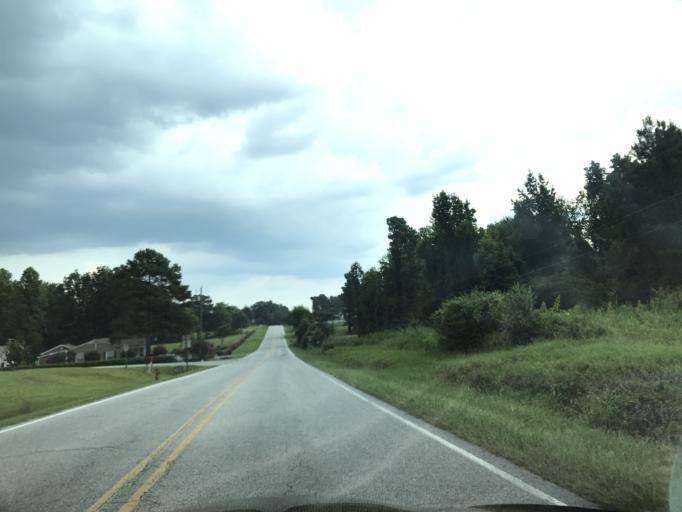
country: US
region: North Carolina
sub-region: Johnston County
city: Four Oaks
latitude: 35.5103
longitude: -78.4747
